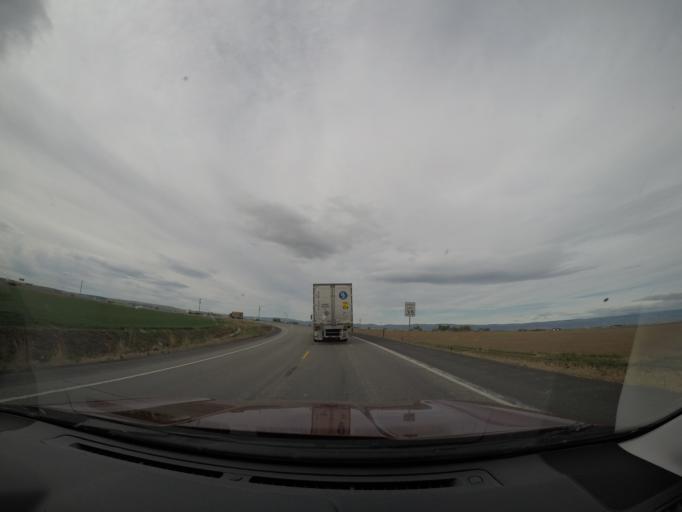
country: US
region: Washington
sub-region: Grant County
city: Quincy
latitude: 47.0905
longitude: -119.8619
